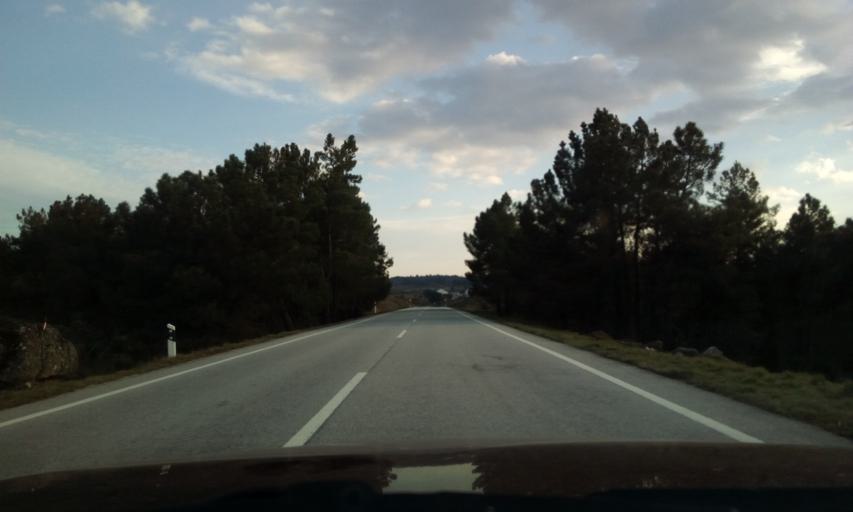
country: PT
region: Guarda
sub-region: Pinhel
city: Pinhel
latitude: 40.6789
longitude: -6.9503
